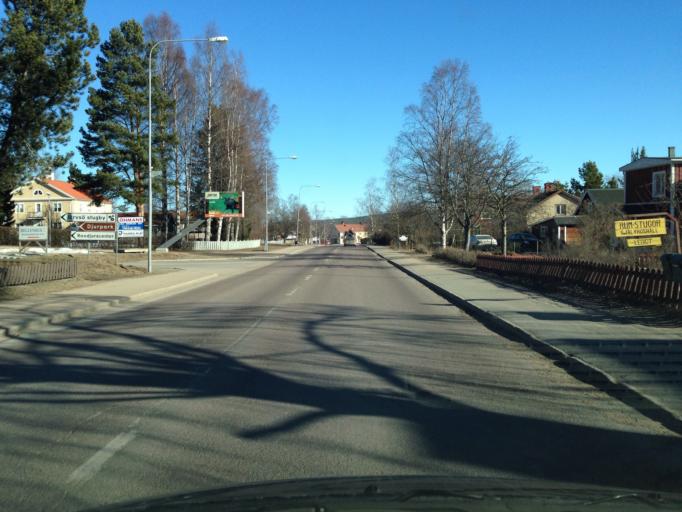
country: SE
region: Gaevleborg
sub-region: Ljusdals Kommun
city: Jaervsoe
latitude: 61.7109
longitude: 16.1662
